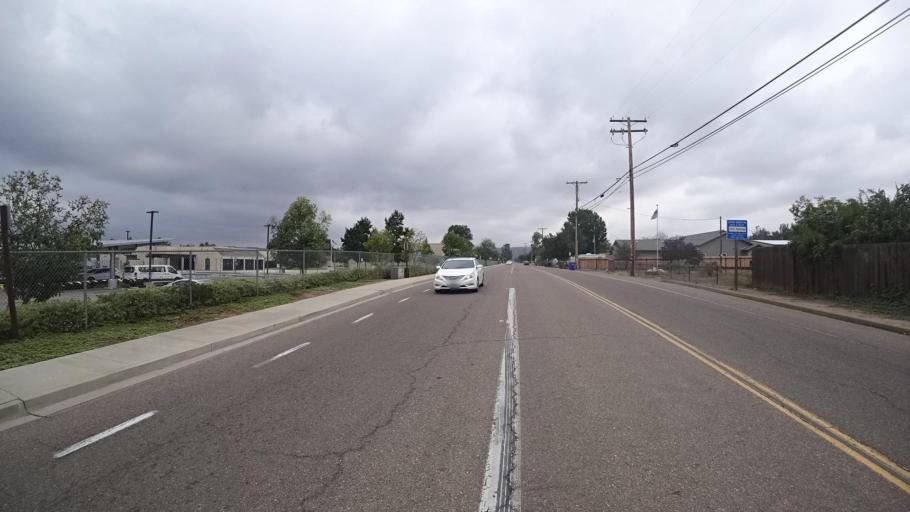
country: US
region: California
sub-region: San Diego County
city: Ramona
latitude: 33.0258
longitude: -116.8792
